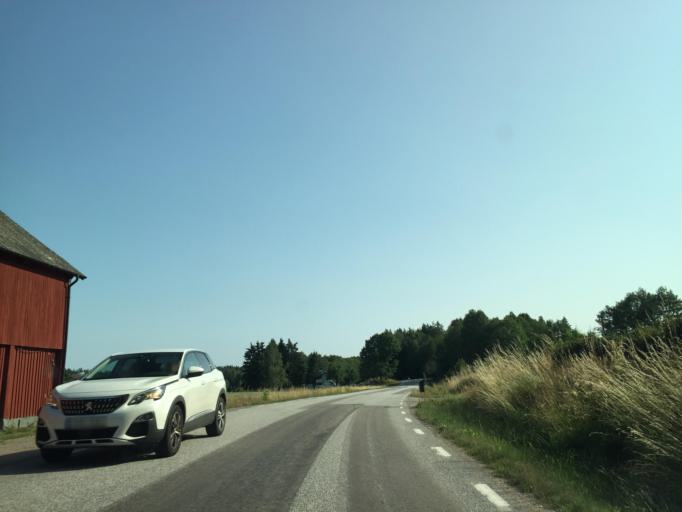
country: SE
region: Vaestra Goetaland
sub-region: Trollhattan
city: Trollhattan
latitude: 58.3069
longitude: 12.2539
